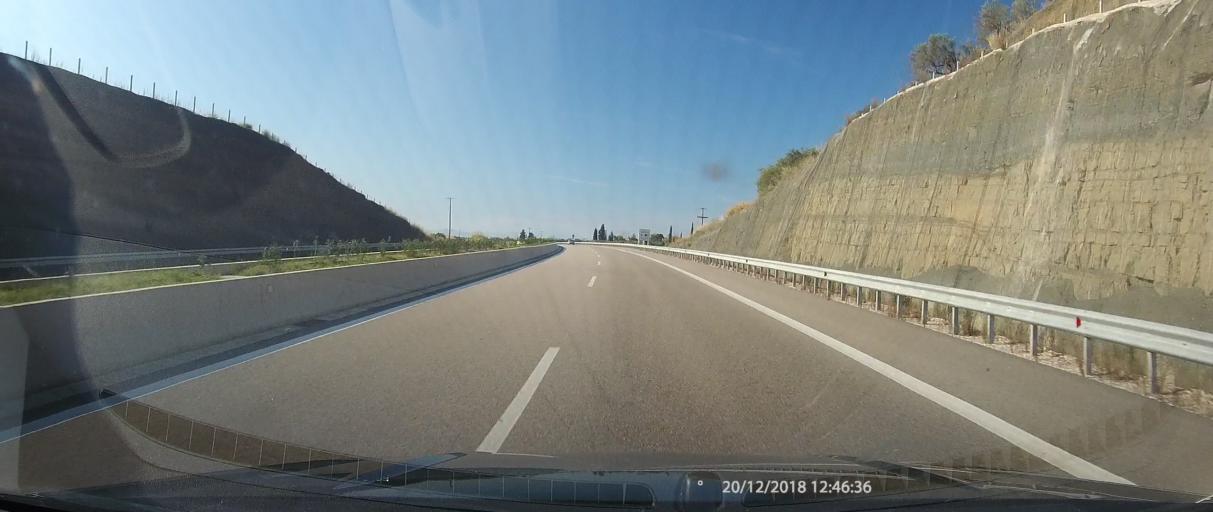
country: GR
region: West Greece
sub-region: Nomos Aitolias kai Akarnanias
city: Mesolongi
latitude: 38.3933
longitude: 21.4686
